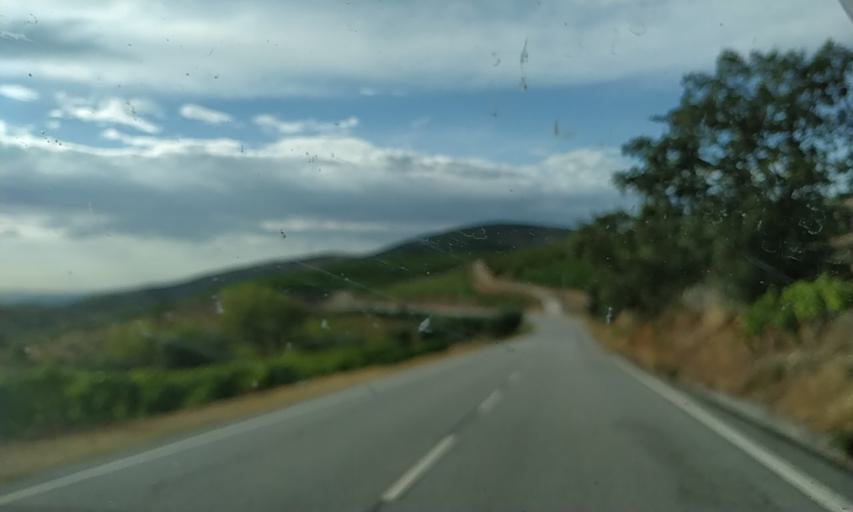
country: PT
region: Viseu
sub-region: Sao Joao da Pesqueira
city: Sao Joao da Pesqueira
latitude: 41.0859
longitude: -7.4653
